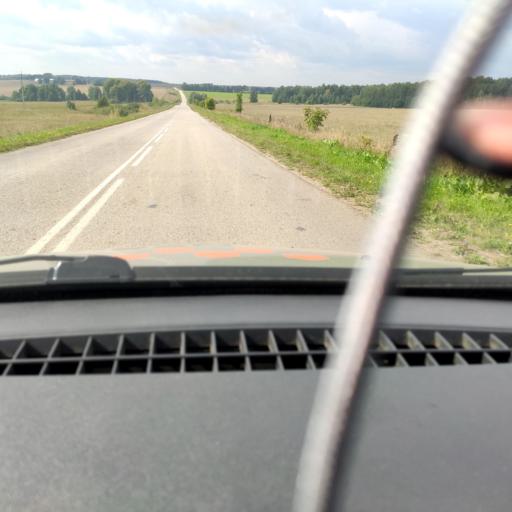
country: RU
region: Bashkortostan
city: Iglino
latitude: 54.7548
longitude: 56.5800
